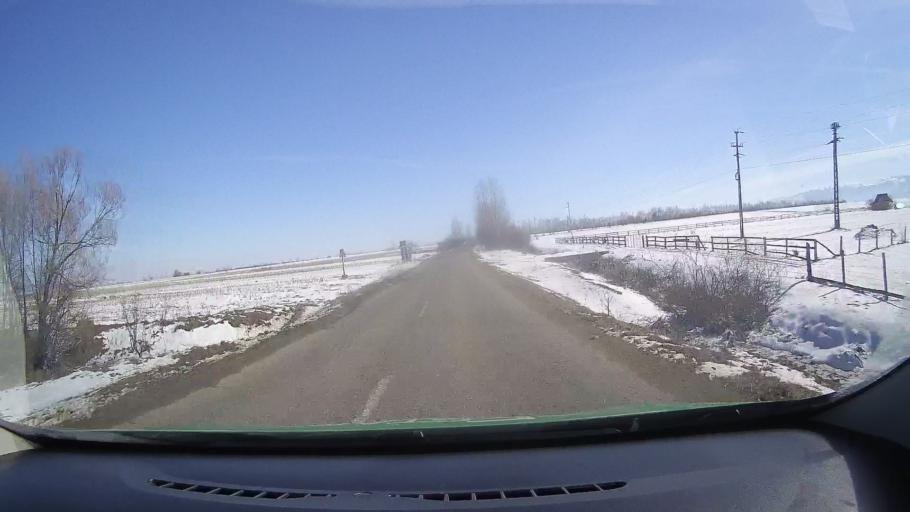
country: RO
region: Brasov
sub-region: Comuna Dragus
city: Dragus
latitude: 45.7532
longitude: 24.7446
